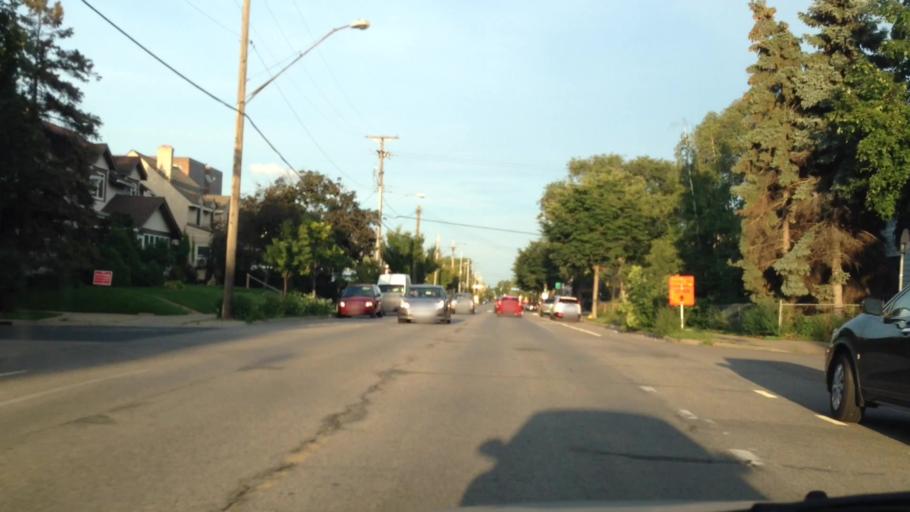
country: US
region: Minnesota
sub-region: Hennepin County
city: Minneapolis
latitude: 44.9377
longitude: -93.2923
